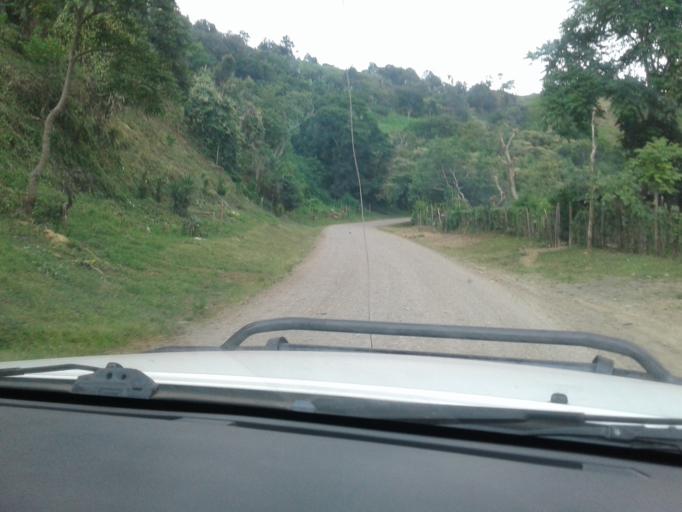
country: NI
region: Matagalpa
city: San Ramon
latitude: 12.9142
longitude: -85.7889
